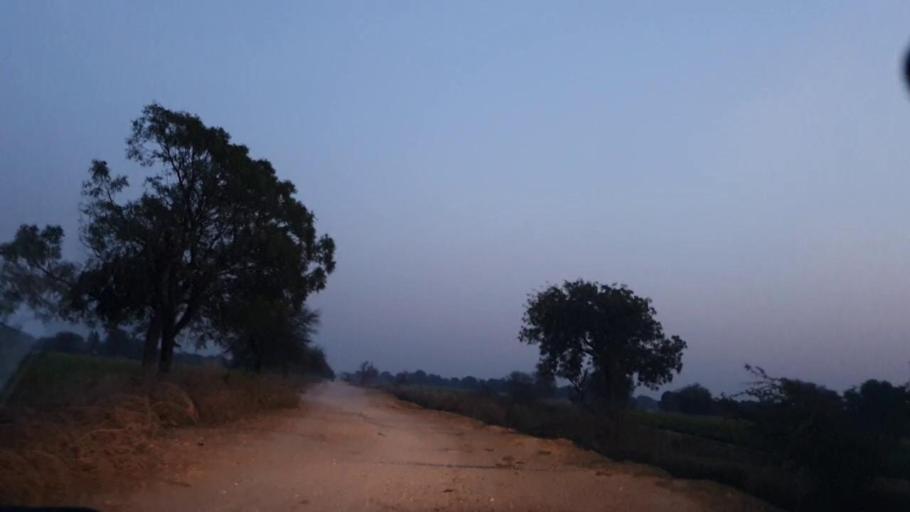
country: PK
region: Sindh
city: Tando Ghulam Ali
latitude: 25.1066
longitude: 68.9086
